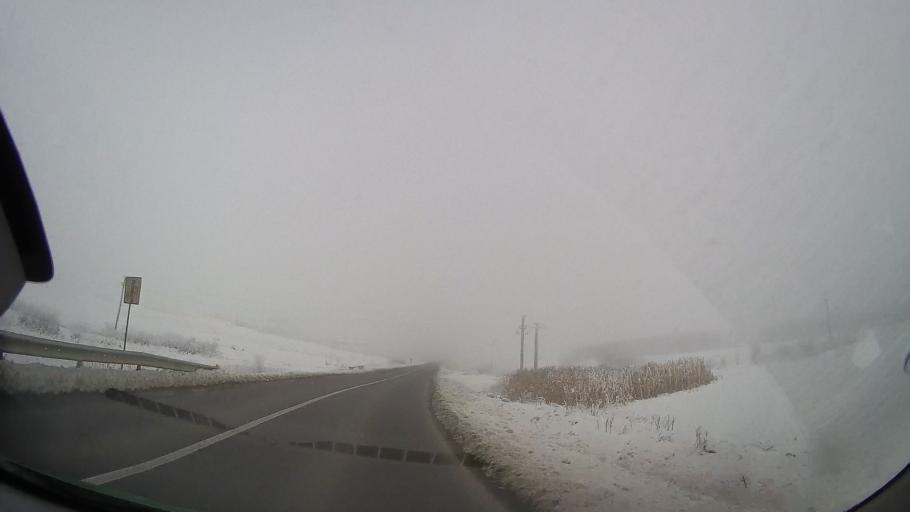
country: RO
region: Iasi
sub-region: Comuna Stolniceni-Prajescu
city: Stolniceni-Prajescu
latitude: 47.1888
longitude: 26.7365
